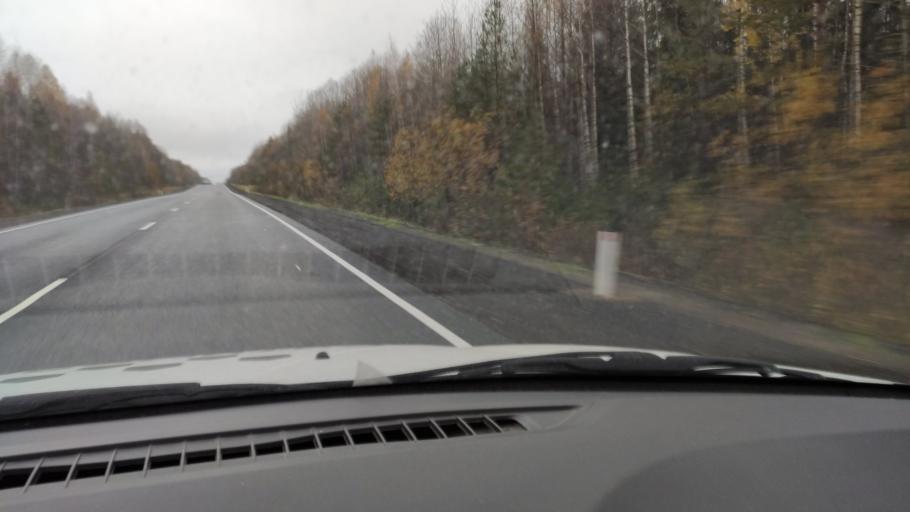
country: RU
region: Kirov
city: Chernaya Kholunitsa
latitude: 58.8815
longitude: 51.4320
